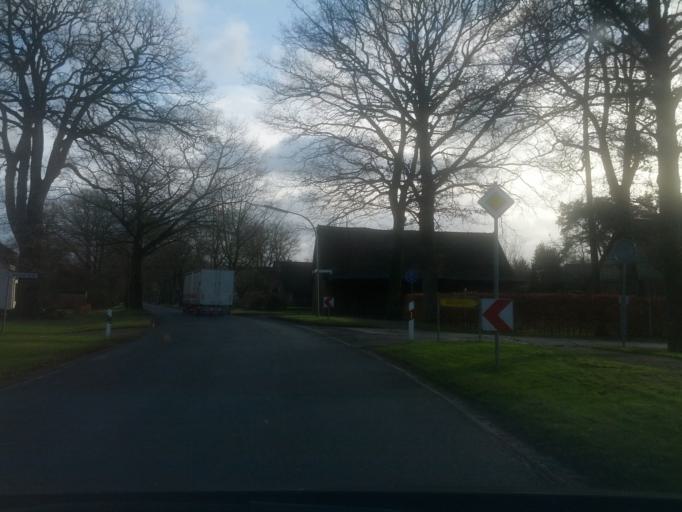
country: DE
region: Lower Saxony
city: Helvesiek
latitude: 53.2171
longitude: 9.4851
